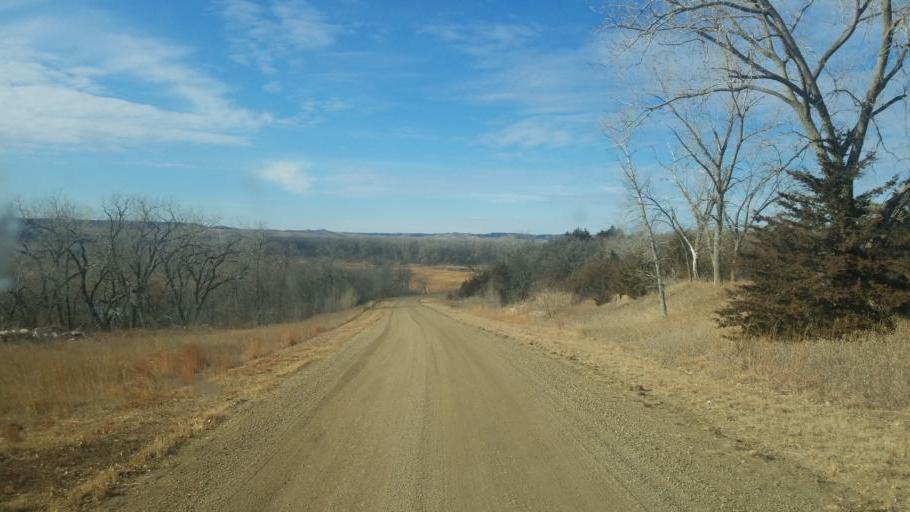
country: US
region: South Dakota
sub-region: Charles Mix County
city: Wagner
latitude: 42.9336
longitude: -98.4157
